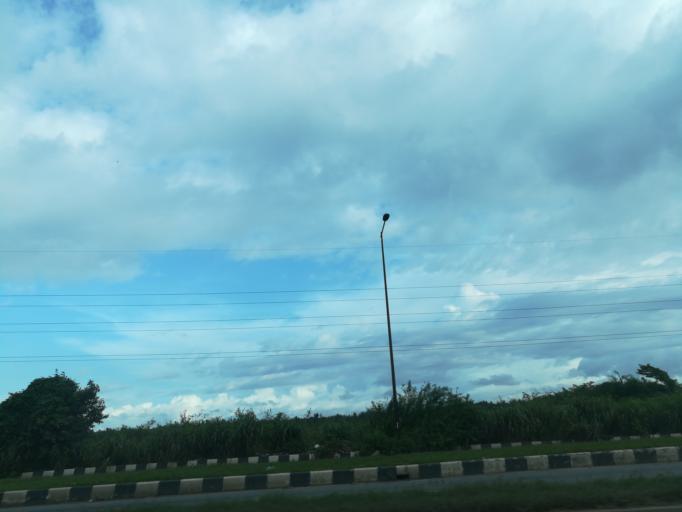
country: NG
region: Lagos
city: Ebute Ikorodu
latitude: 6.6207
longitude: 3.4509
